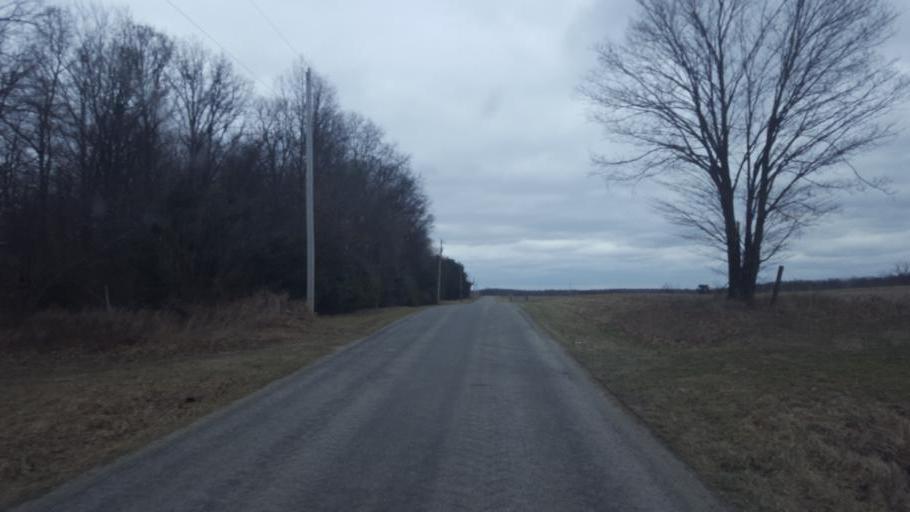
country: US
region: Ohio
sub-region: Crawford County
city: Galion
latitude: 40.6676
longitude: -82.7235
